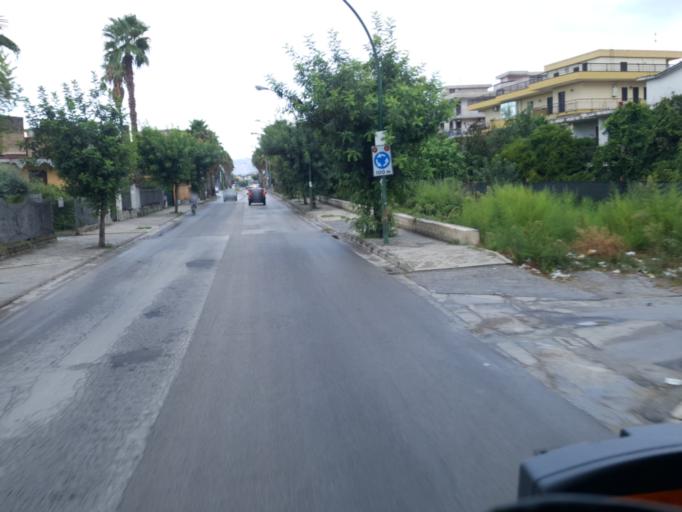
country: IT
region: Campania
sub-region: Provincia di Napoli
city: Palma Campania
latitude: 40.8666
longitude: 14.5483
